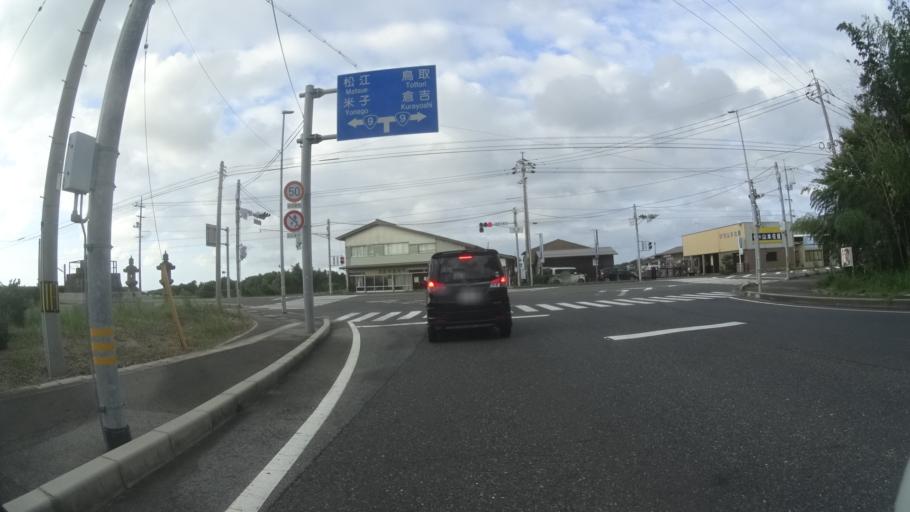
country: JP
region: Tottori
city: Kurayoshi
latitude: 35.5212
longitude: 133.5997
